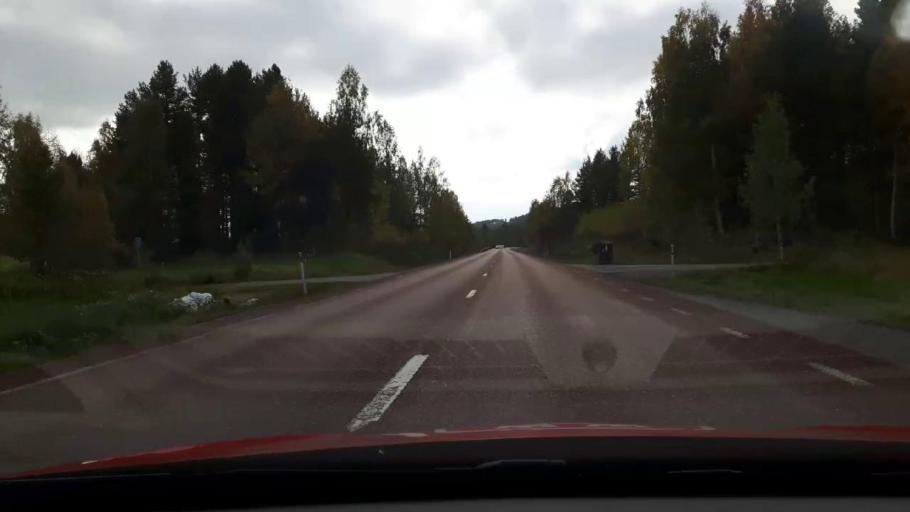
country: SE
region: Gaevleborg
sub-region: Bollnas Kommun
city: Arbra
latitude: 61.6076
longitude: 16.2955
